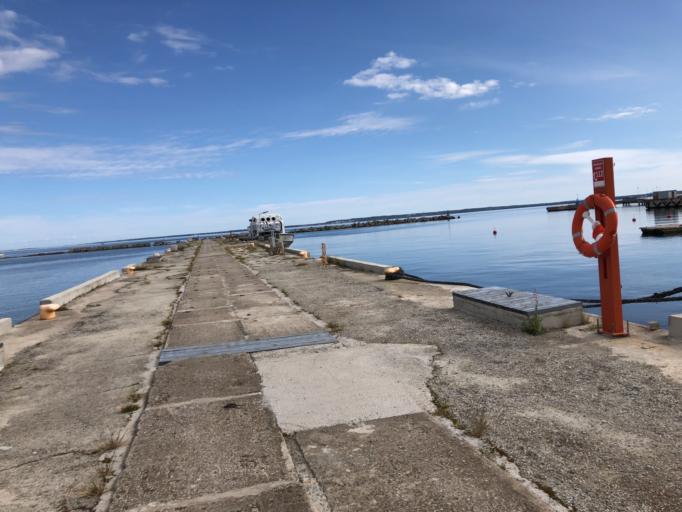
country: EE
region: Harju
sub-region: Tallinna linn
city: Tallinn
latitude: 59.4532
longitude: 24.7286
